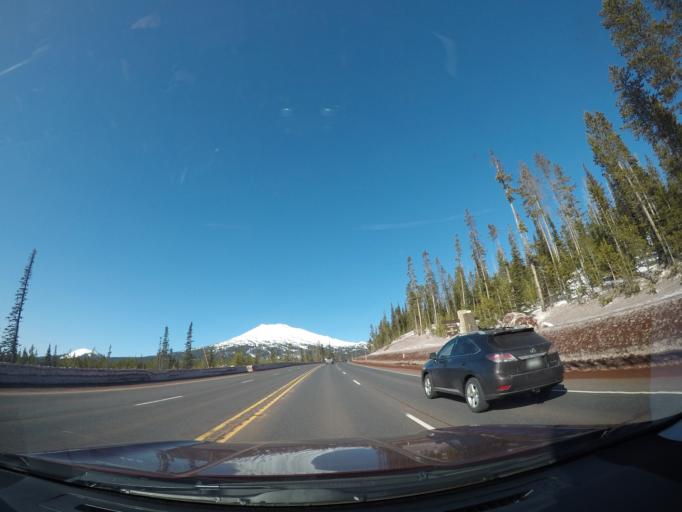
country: US
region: Oregon
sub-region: Deschutes County
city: Sunriver
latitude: 43.9828
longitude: -121.6255
